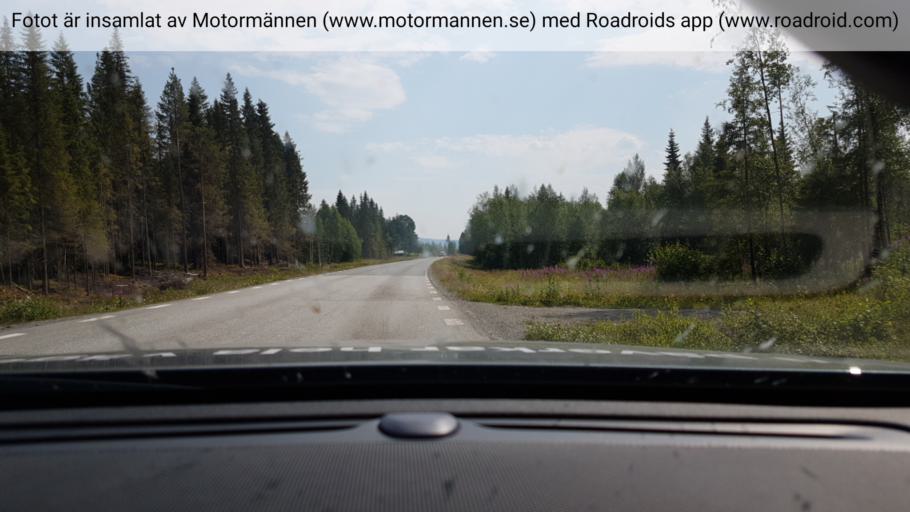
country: SE
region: Vaesterbotten
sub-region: Vilhelmina Kommun
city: Sjoberg
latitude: 65.4758
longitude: 16.0089
